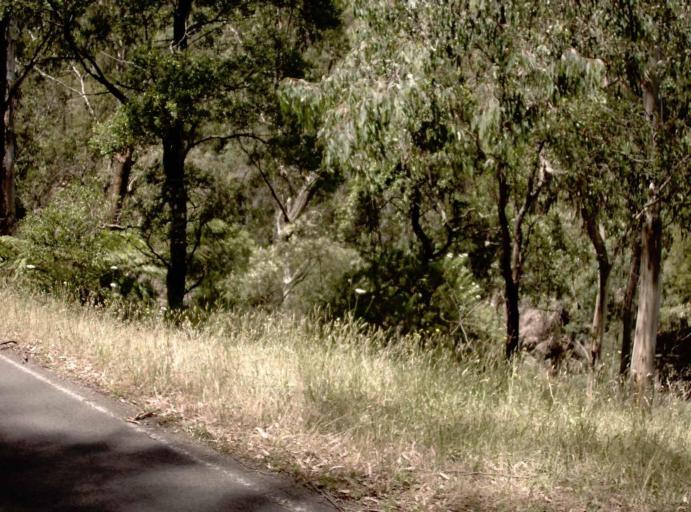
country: AU
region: Victoria
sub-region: Latrobe
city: Traralgon
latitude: -37.9526
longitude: 146.4286
